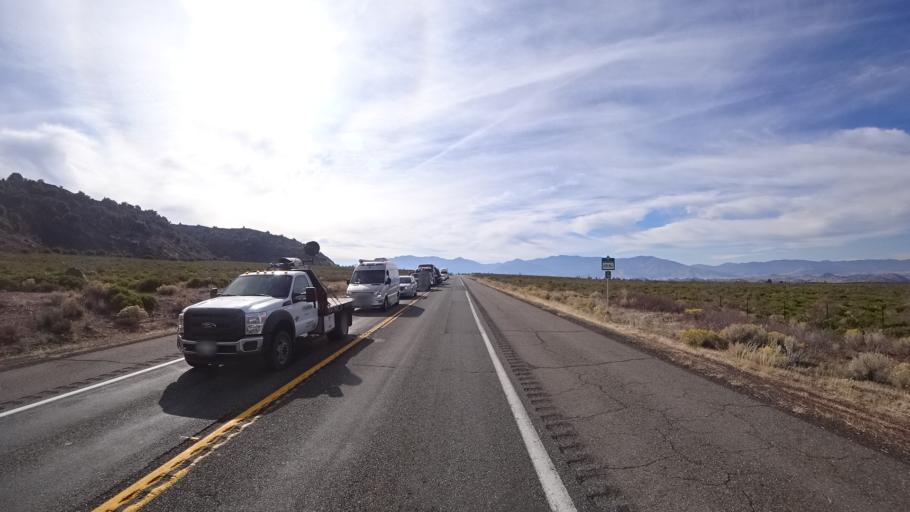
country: US
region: California
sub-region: Siskiyou County
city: Weed
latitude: 41.5163
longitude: -122.3100
